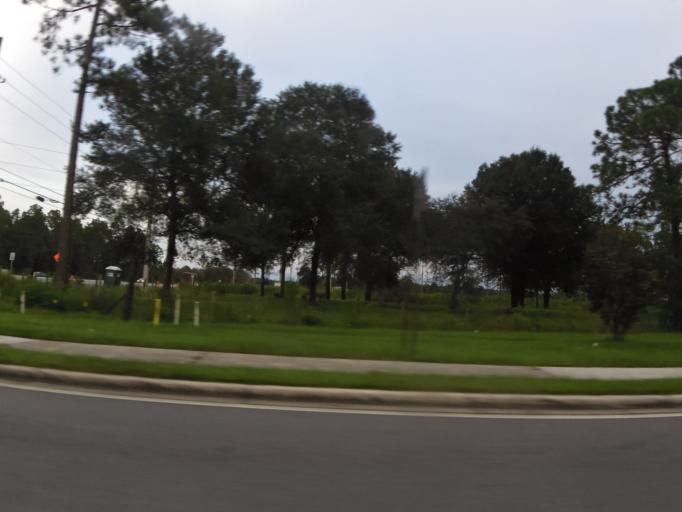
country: US
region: Florida
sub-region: Saint Johns County
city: Fruit Cove
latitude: 30.1032
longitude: -81.5397
